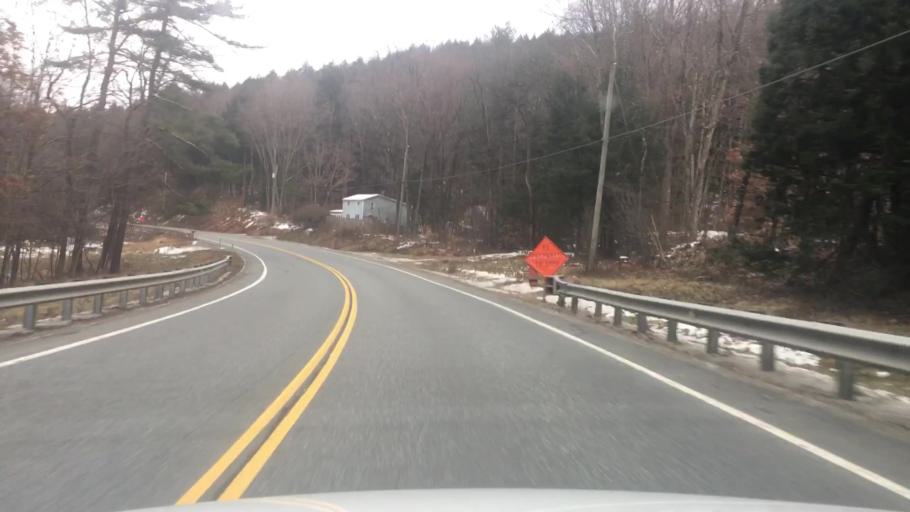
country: US
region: New Hampshire
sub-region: Cheshire County
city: Westmoreland
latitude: 42.9899
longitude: -72.4283
